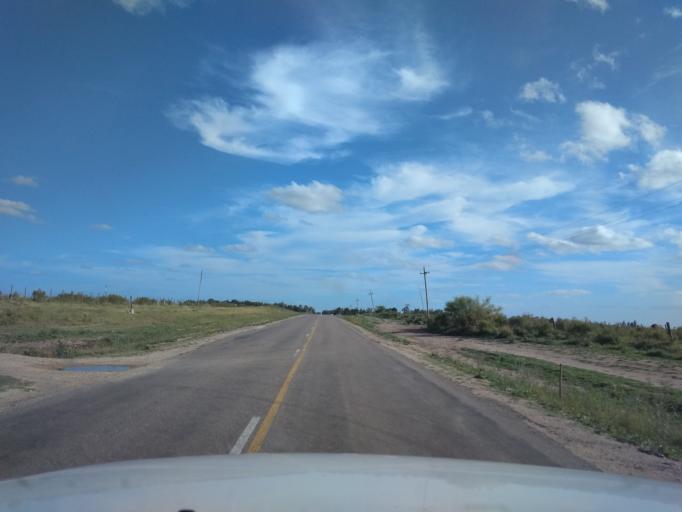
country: UY
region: Canelones
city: San Ramon
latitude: -34.2319
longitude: -55.9283
